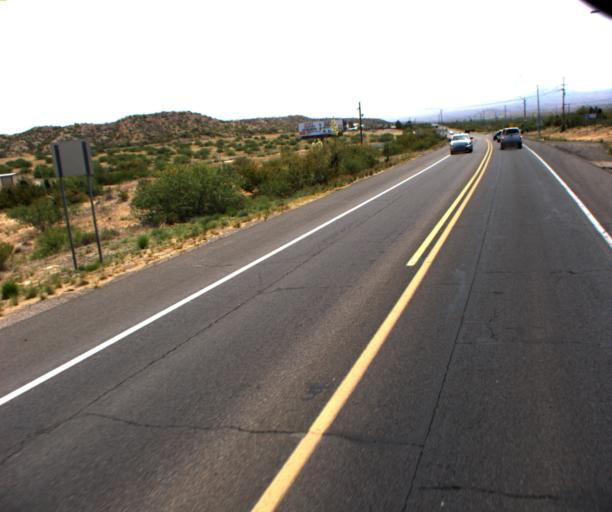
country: US
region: Arizona
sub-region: Gila County
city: Globe
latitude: 33.3746
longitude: -110.7411
